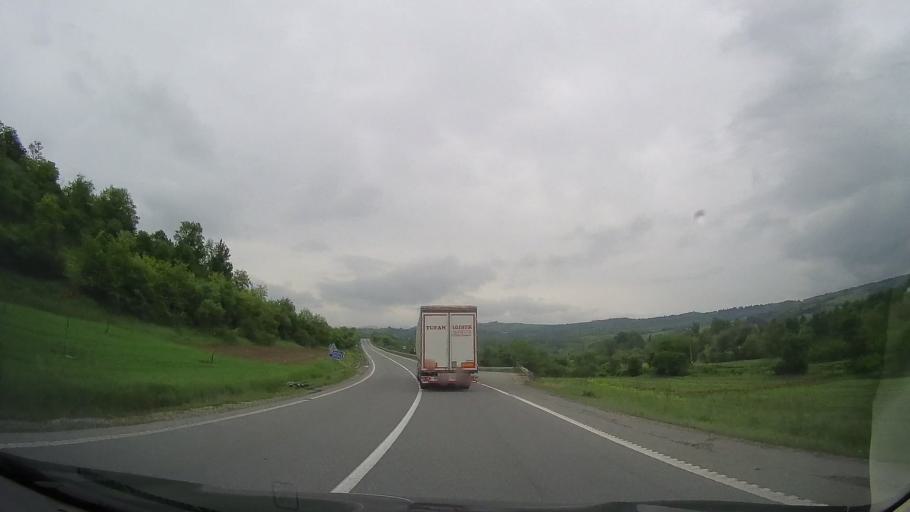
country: RO
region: Caras-Severin
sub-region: Comuna Cornea
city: Cornea
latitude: 45.0078
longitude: 22.3203
